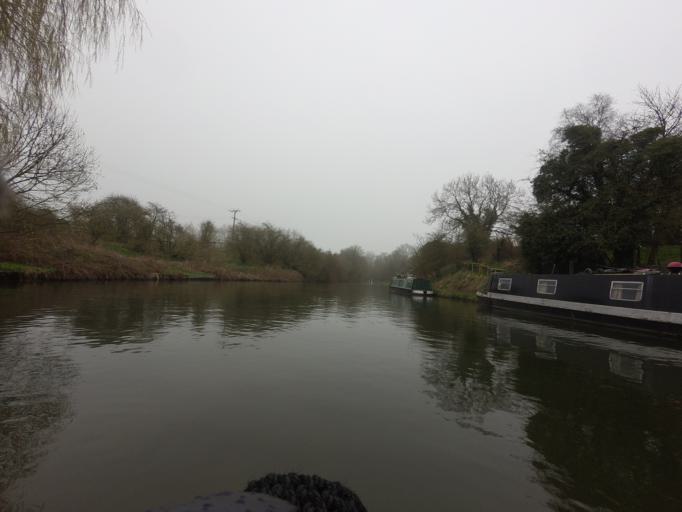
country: GB
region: England
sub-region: Hertfordshire
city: Tring
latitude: 51.8130
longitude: -0.6466
